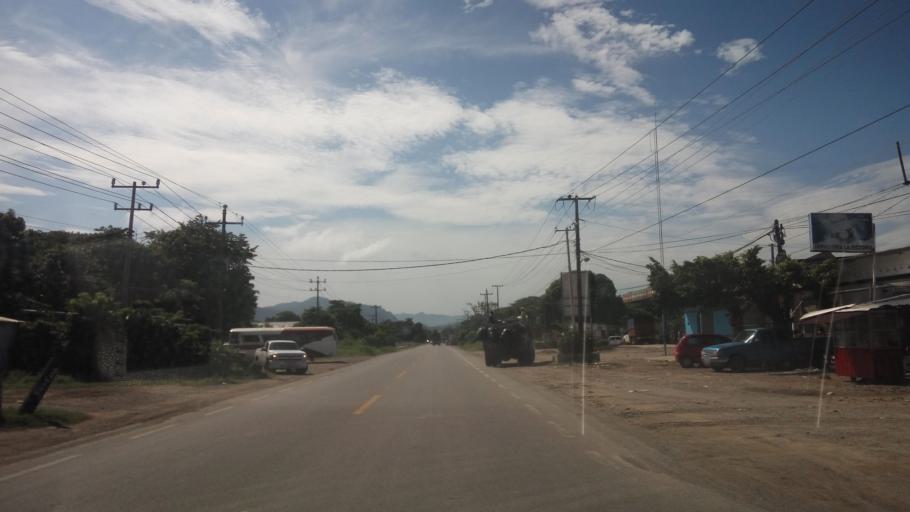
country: MX
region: Tabasco
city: Teapa
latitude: 17.5744
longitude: -92.9582
